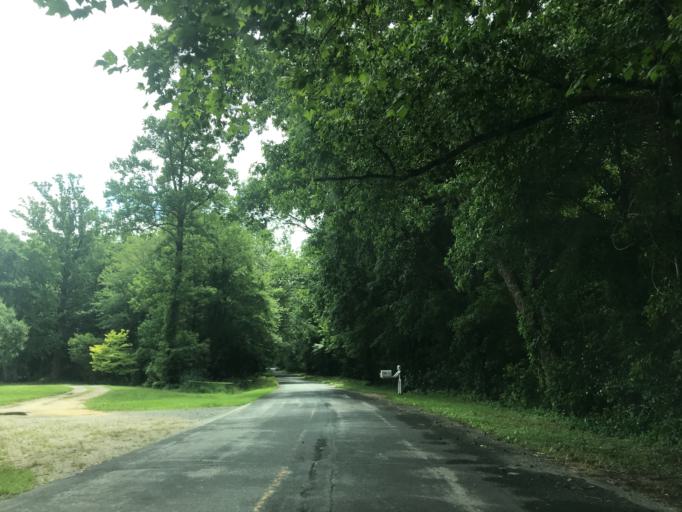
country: US
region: Maryland
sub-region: Caroline County
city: Ridgely
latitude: 38.9210
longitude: -75.9701
